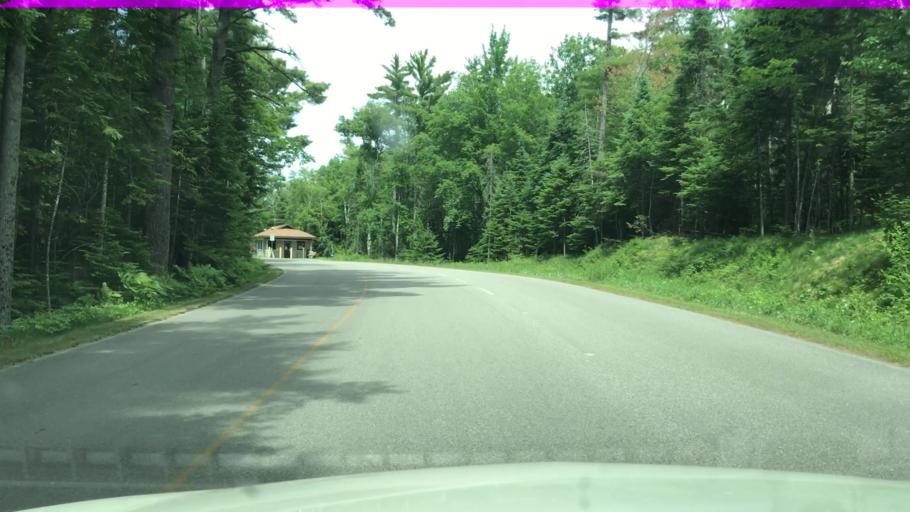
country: US
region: Michigan
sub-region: Schoolcraft County
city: Manistique
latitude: 45.9429
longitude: -86.3327
